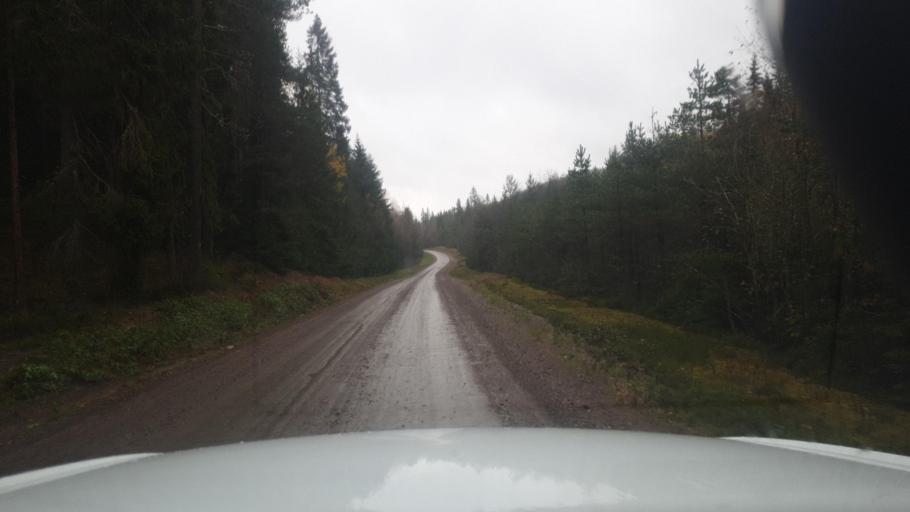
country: SE
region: Vaermland
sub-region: Eda Kommun
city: Charlottenberg
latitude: 60.0565
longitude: 12.5581
